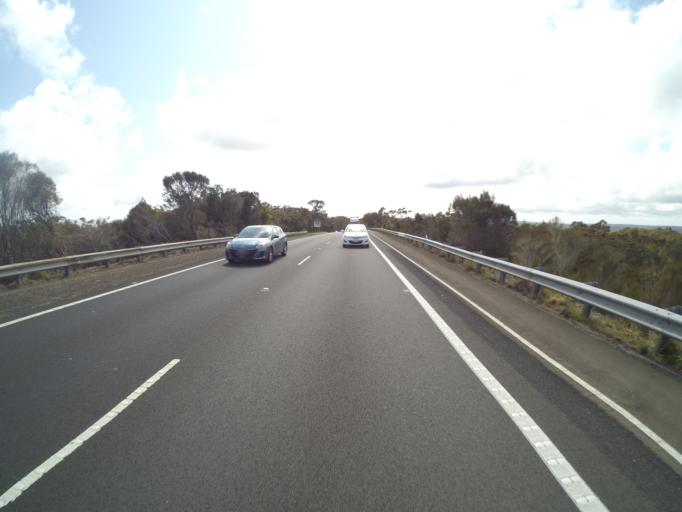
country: AU
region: New South Wales
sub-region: Wollongong
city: Helensburgh
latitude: -34.1470
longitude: 150.9925
